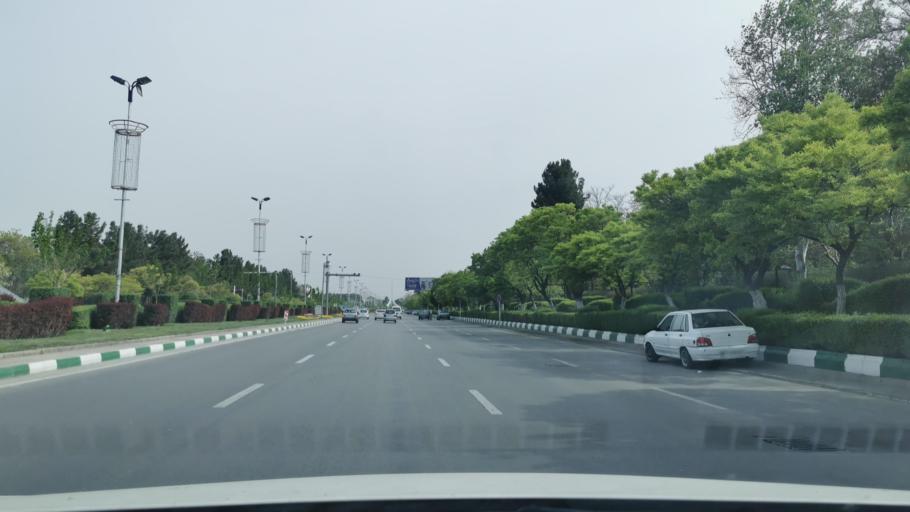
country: IR
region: Razavi Khorasan
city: Mashhad
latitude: 36.2485
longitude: 59.6181
